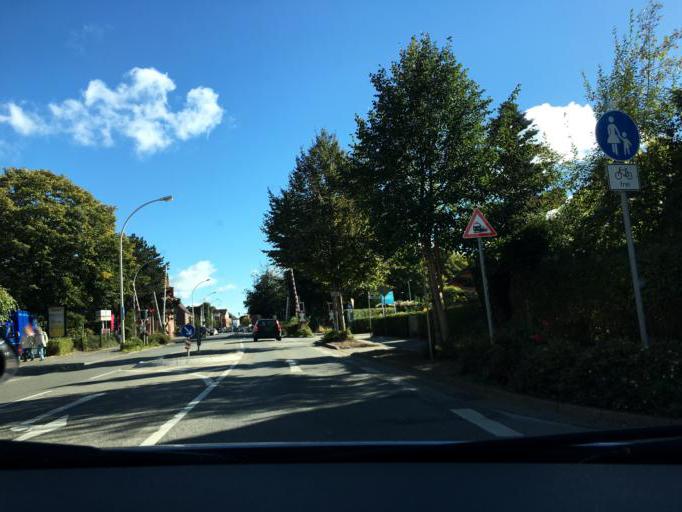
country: DE
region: Schleswig-Holstein
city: Kronshagen
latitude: 54.3317
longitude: 10.0818
